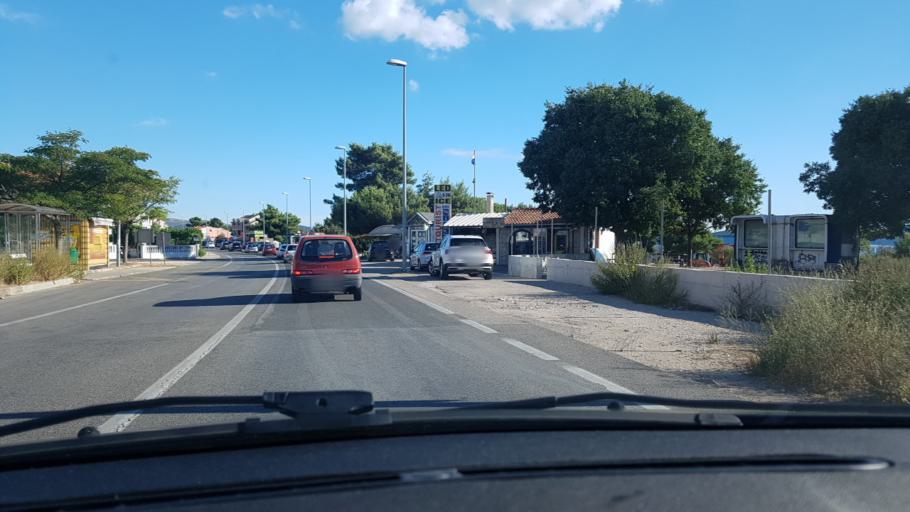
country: HR
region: Sibensko-Kniniska
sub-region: Grad Sibenik
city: Brodarica
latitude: 43.6948
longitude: 15.9032
